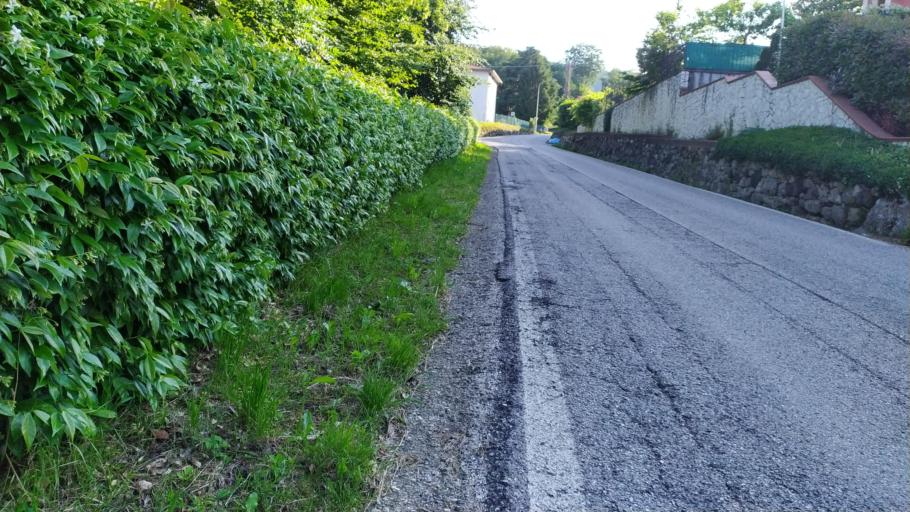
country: IT
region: Veneto
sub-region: Provincia di Vicenza
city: Schio
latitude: 45.6876
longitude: 11.3389
